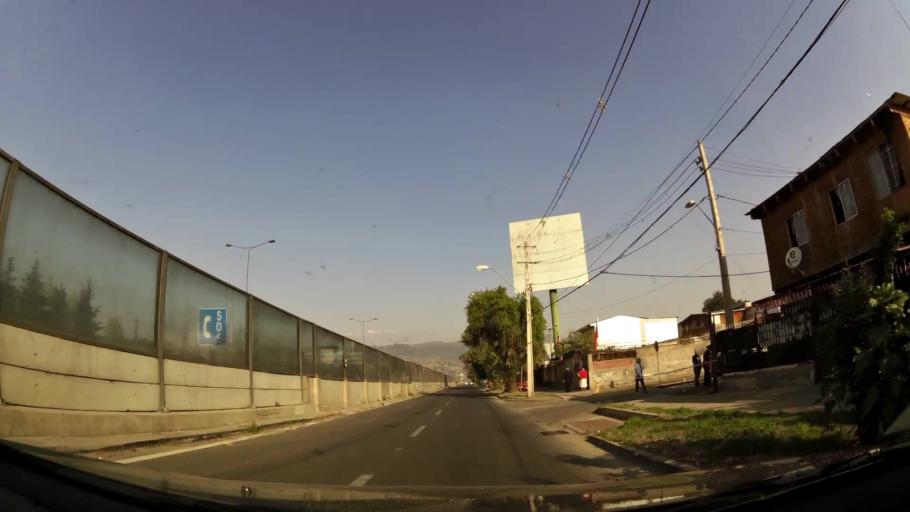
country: CL
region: Santiago Metropolitan
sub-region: Provincia de Santiago
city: Santiago
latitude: -33.3875
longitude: -70.6351
